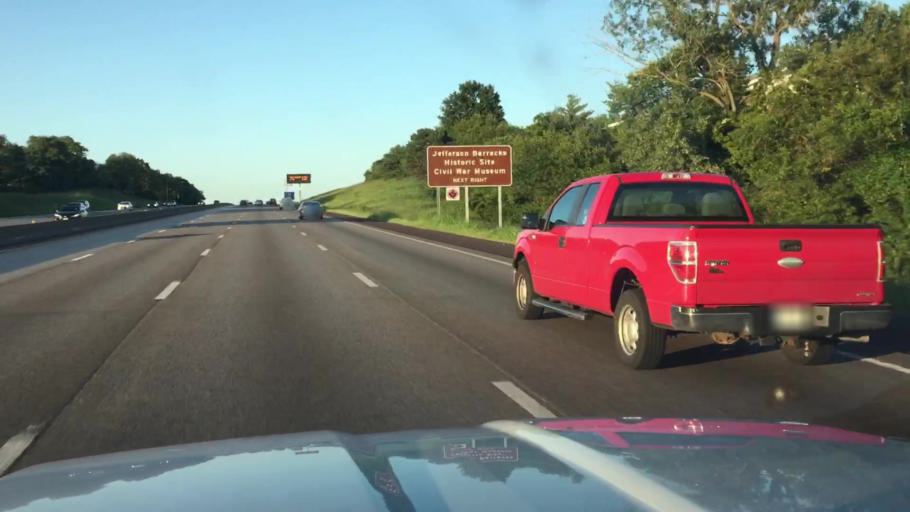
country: US
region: Missouri
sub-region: Saint Louis County
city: Saint George
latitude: 38.5268
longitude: -90.3175
